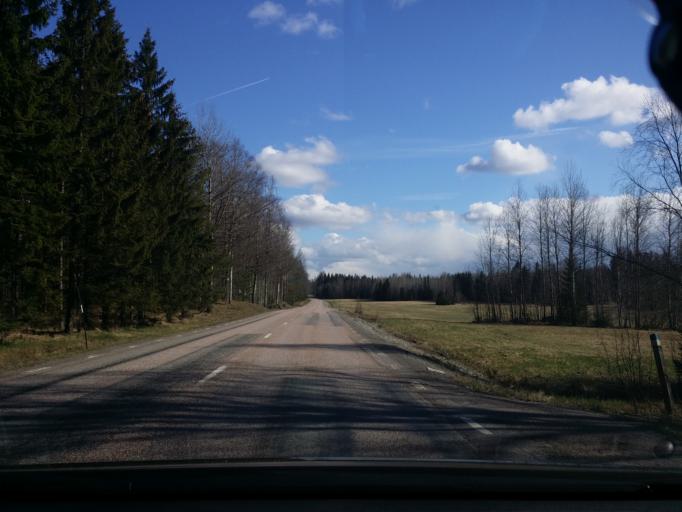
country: SE
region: Vaestmanland
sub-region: Sala Kommun
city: Sala
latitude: 59.9802
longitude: 16.4901
